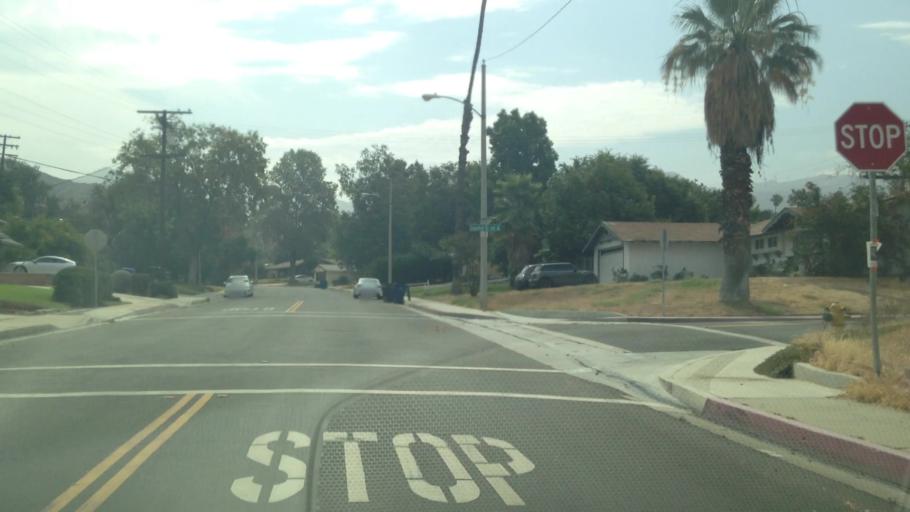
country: US
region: California
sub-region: Riverside County
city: Highgrove
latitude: 33.9881
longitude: -117.3266
